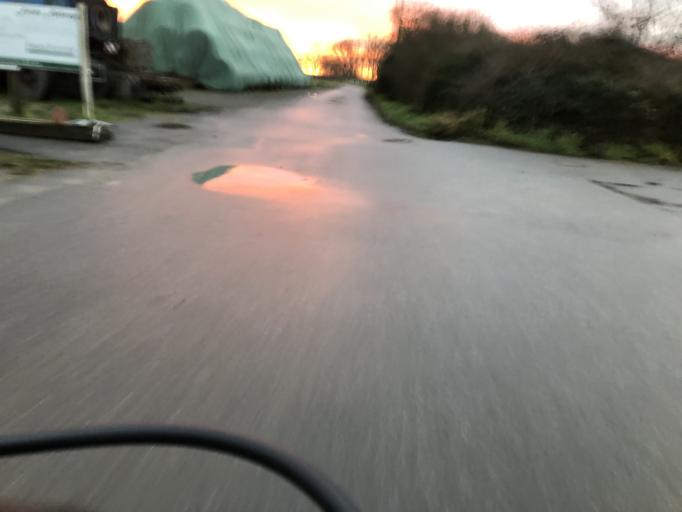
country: DE
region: Baden-Wuerttemberg
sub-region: Karlsruhe Region
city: Reilingen
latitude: 49.2914
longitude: 8.5847
